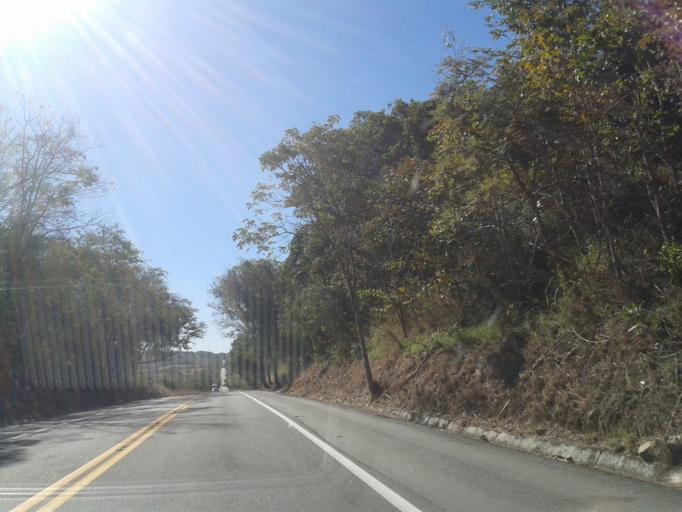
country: BR
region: Goias
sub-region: Goias
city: Goias
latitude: -15.7157
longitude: -50.1895
